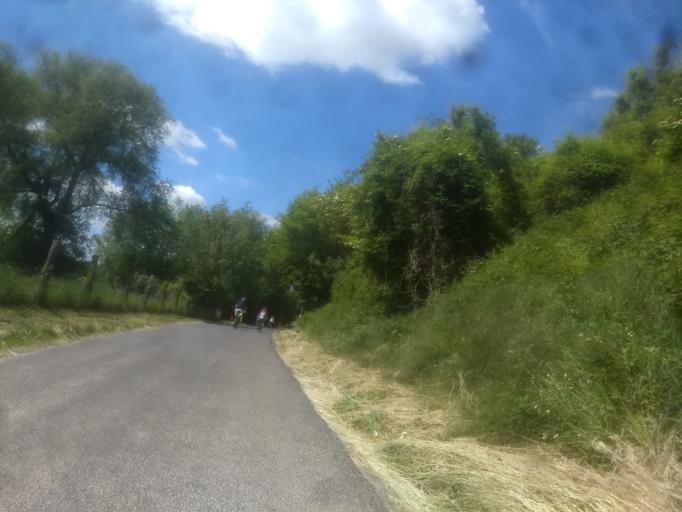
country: FR
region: Nord-Pas-de-Calais
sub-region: Departement du Pas-de-Calais
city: Riviere
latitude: 50.2410
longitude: 2.7073
